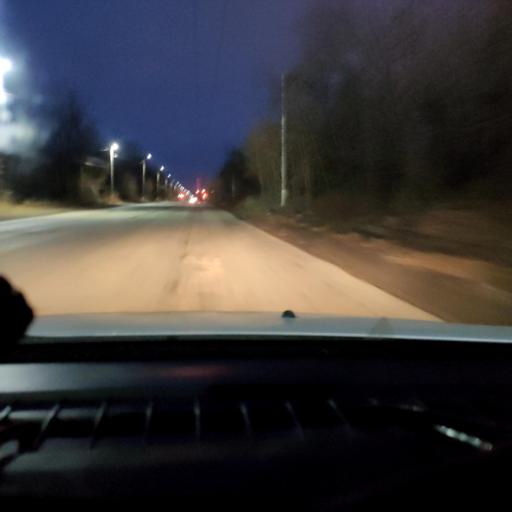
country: RU
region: Samara
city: Novokuybyshevsk
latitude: 53.0810
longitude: 49.9346
